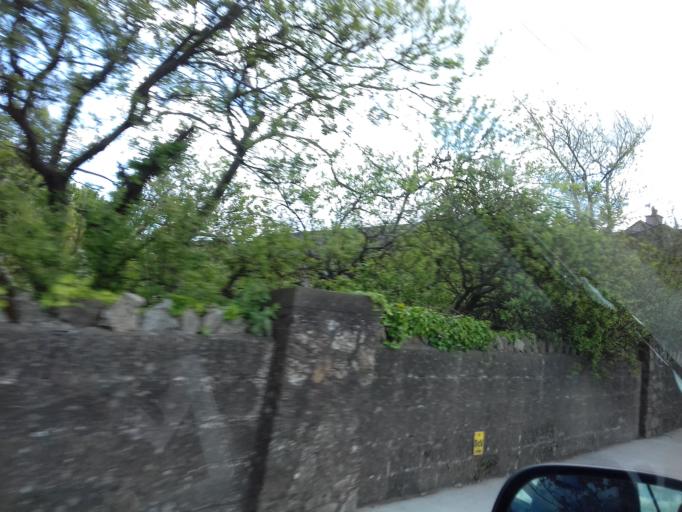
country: IE
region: Leinster
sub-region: Loch Garman
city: Loch Garman
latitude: 52.3450
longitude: -6.4555
